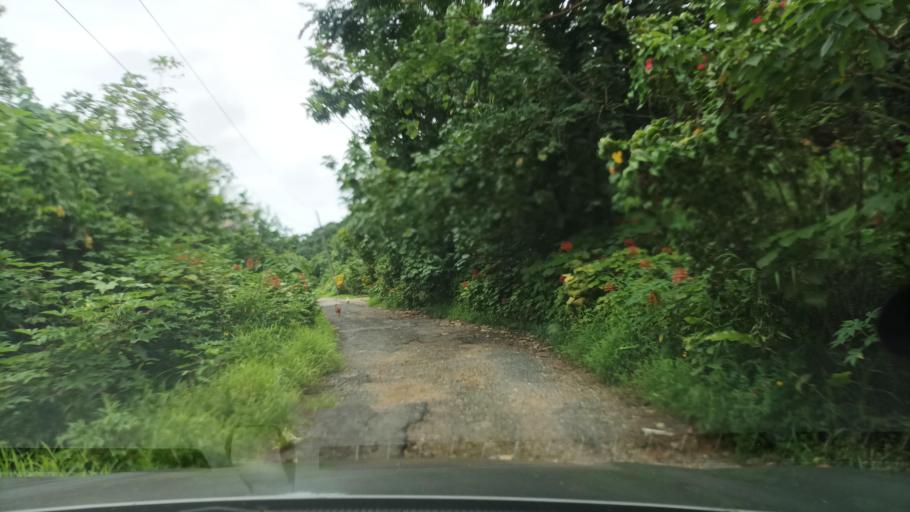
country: FM
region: Pohnpei
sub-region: Kolonia Municipality
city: Kolonia
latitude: 6.9409
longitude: 158.2707
